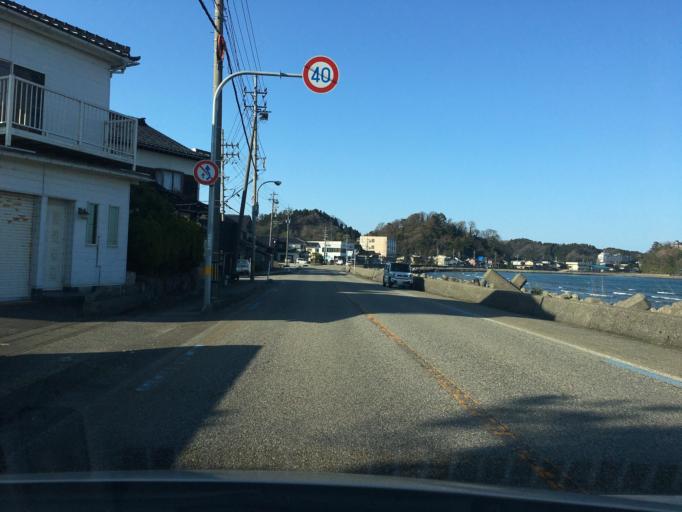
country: JP
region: Toyama
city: Himi
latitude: 36.8757
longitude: 136.9844
